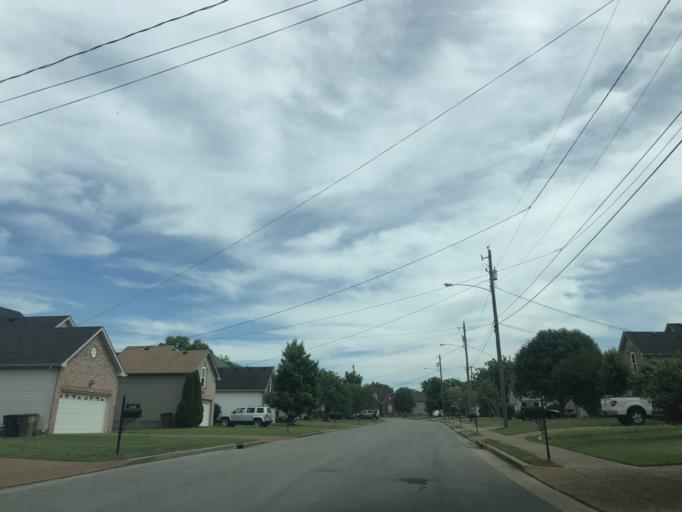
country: US
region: Tennessee
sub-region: Davidson County
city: Nashville
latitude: 36.2135
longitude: -86.8135
